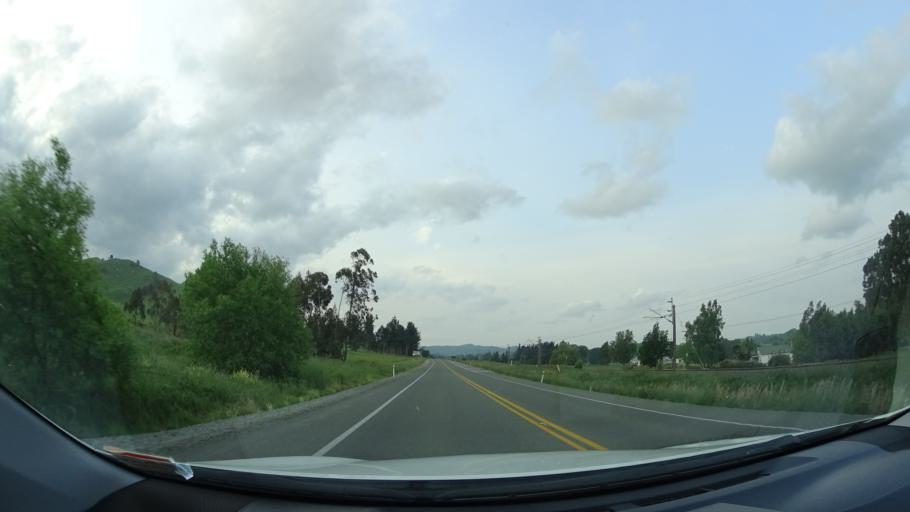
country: NZ
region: Manawatu-Wanganui
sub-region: Ruapehu District
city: Waiouru
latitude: -39.7293
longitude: 175.8433
